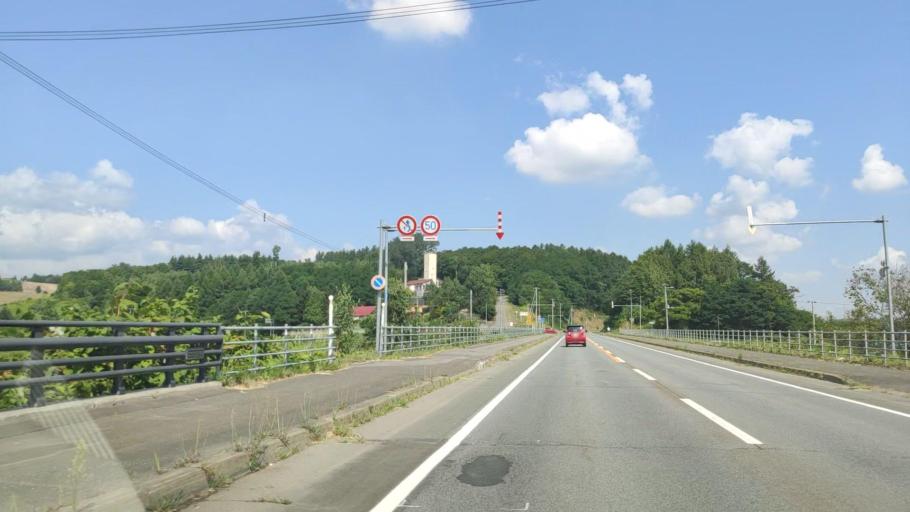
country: JP
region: Hokkaido
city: Shimo-furano
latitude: 43.4688
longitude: 142.4542
